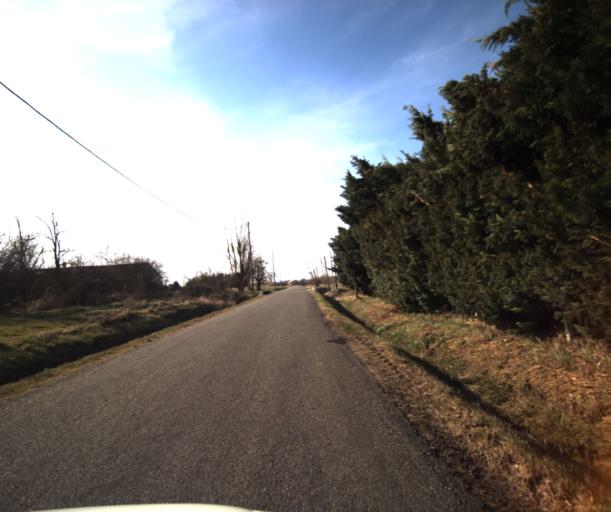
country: FR
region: Midi-Pyrenees
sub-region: Departement du Tarn-et-Garonne
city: Labastide-Saint-Pierre
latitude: 43.9253
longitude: 1.3412
